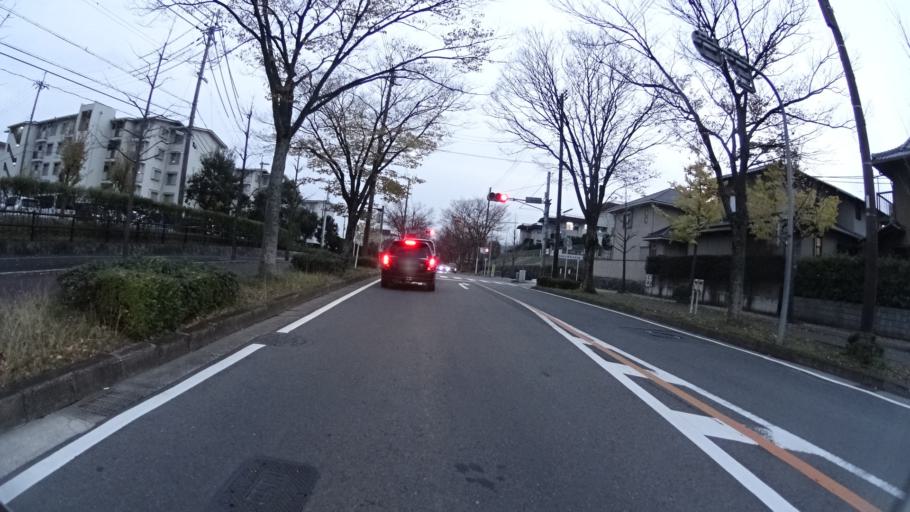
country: JP
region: Kyoto
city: Muko
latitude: 34.9641
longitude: 135.6678
